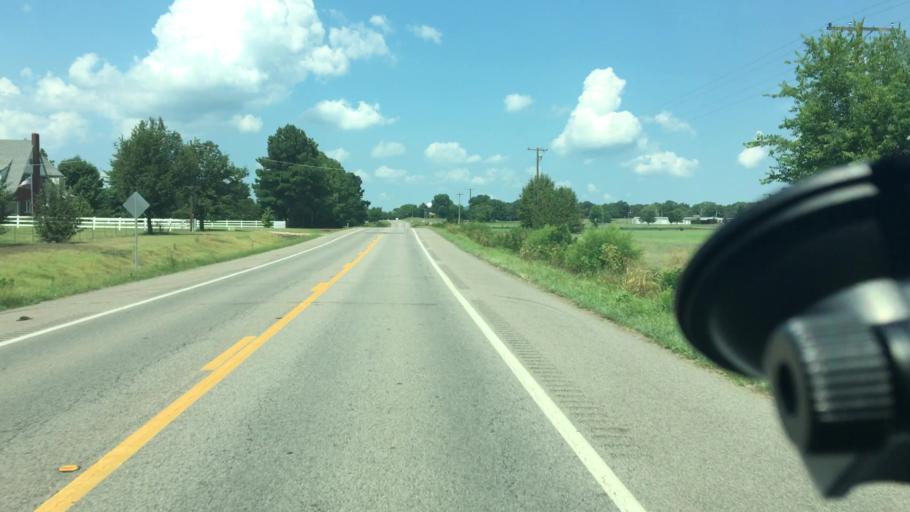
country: US
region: Arkansas
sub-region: Logan County
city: Paris
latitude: 35.2951
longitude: -93.6798
